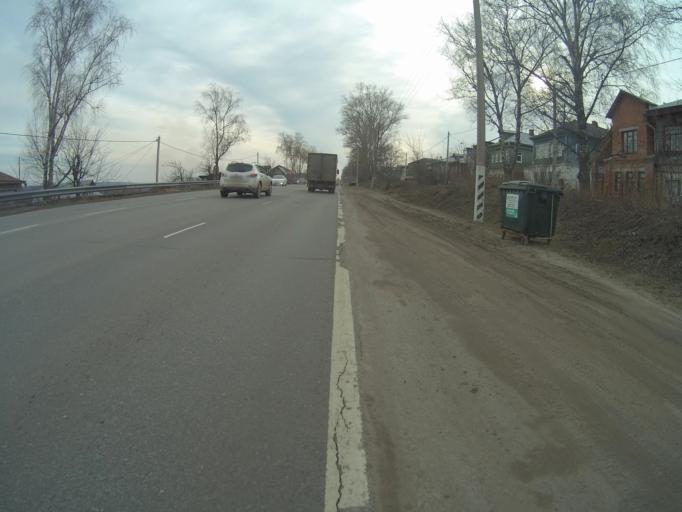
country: RU
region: Vladimir
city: Bogolyubovo
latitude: 56.1924
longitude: 40.5281
